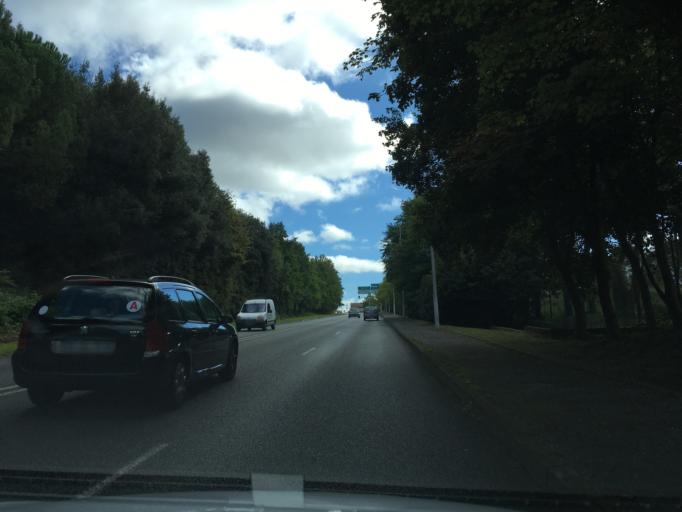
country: FR
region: Aquitaine
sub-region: Departement des Pyrenees-Atlantiques
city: Bayonne
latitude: 43.5040
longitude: -1.4728
